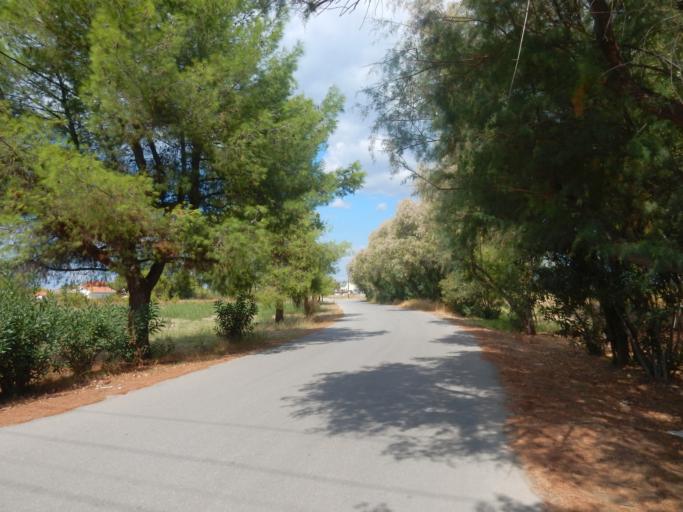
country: GR
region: Attica
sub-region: Nomarchia Anatolikis Attikis
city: Skala Oropou
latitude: 38.3313
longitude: 23.7651
